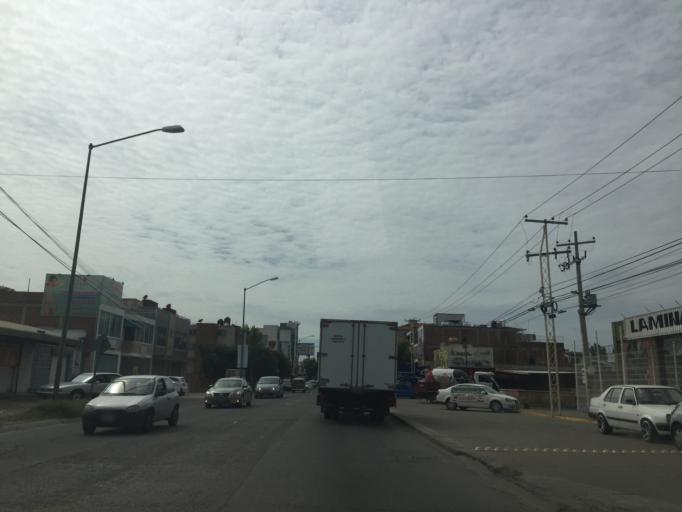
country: MX
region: Guanajuato
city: Leon
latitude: 21.1598
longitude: -101.6835
